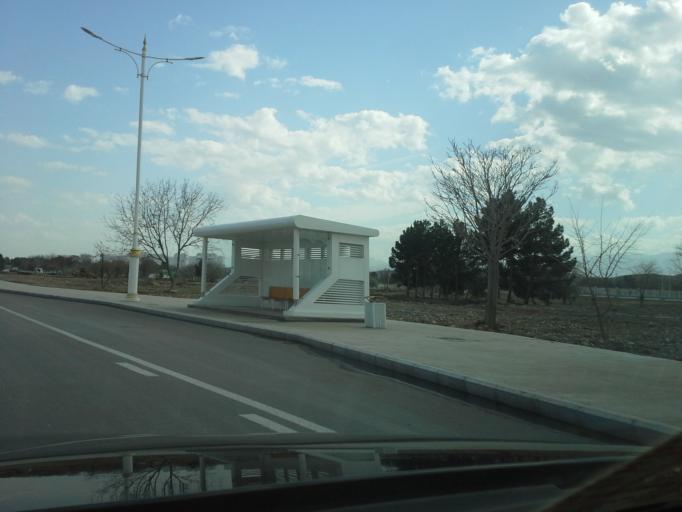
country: TM
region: Ahal
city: Ashgabat
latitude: 37.9636
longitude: 58.3308
